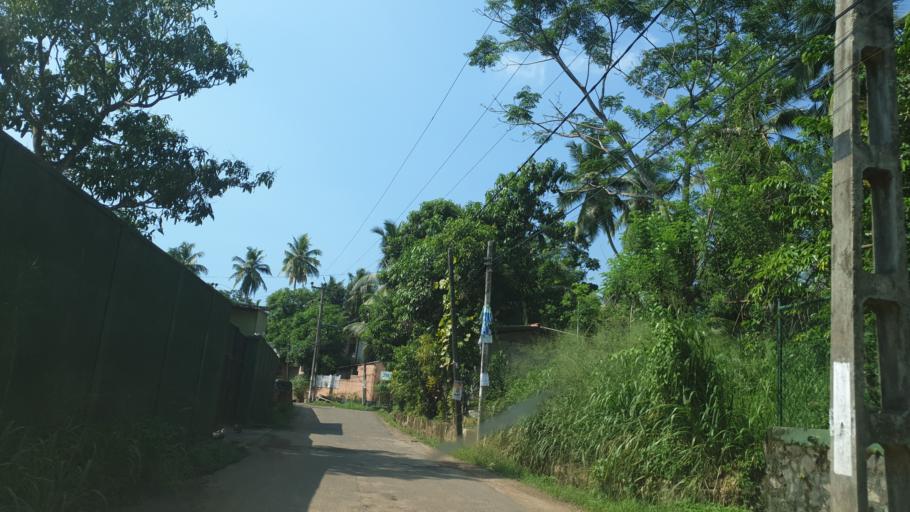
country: LK
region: Western
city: Moratuwa
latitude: 6.7669
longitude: 79.9215
